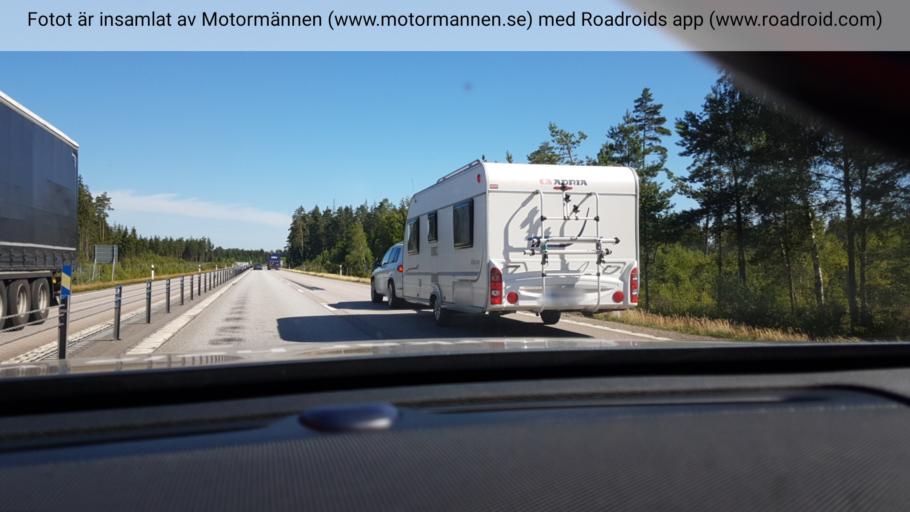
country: SE
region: Kronoberg
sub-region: Ljungby Kommun
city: Lagan
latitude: 56.8792
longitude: 13.9540
